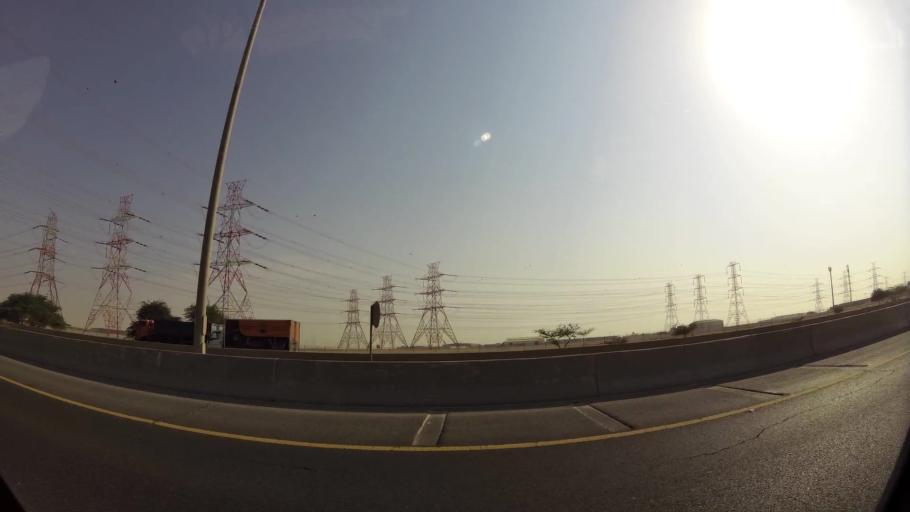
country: KW
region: Al Ahmadi
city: Al Ahmadi
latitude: 29.0105
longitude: 48.0931
